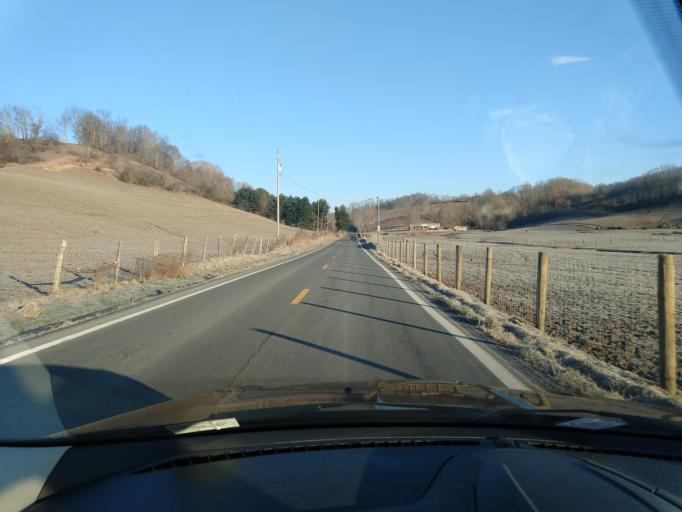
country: US
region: West Virginia
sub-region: Greenbrier County
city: Rainelle
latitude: 37.8648
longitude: -80.7206
